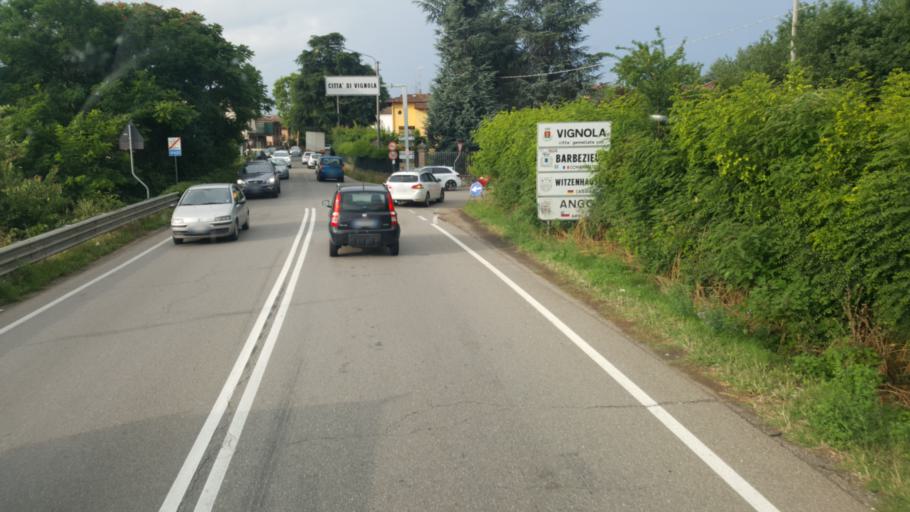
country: IT
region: Emilia-Romagna
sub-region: Provincia di Modena
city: Vignola
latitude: 44.5058
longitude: 11.0229
